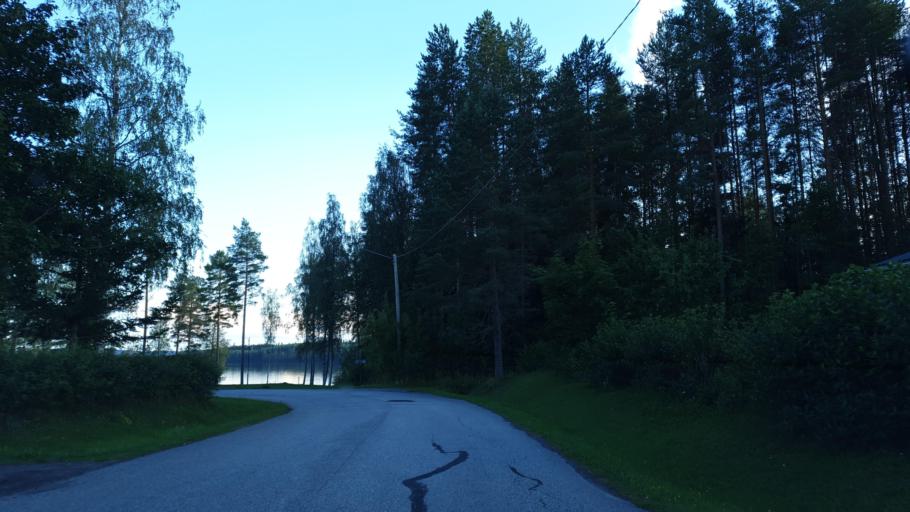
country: FI
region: Northern Savo
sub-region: Koillis-Savo
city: Kaavi
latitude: 62.9754
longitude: 28.4680
